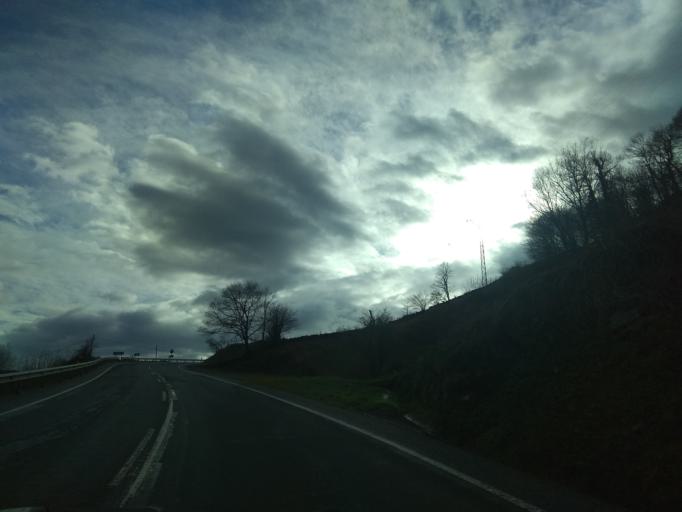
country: ES
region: Cantabria
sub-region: Provincia de Cantabria
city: San Pedro del Romeral
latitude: 43.0840
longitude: -3.8938
